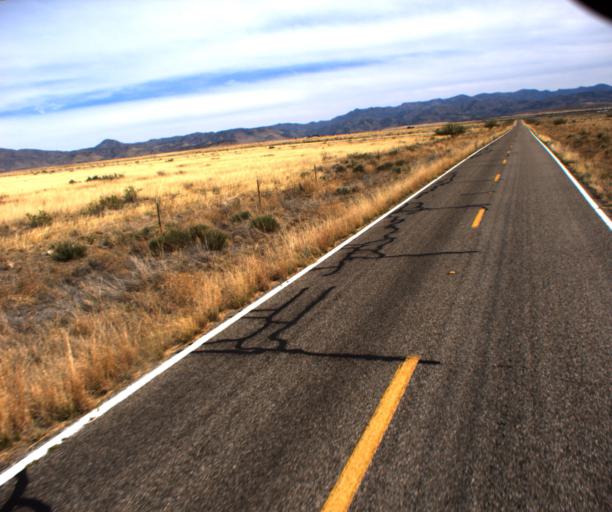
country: US
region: Arizona
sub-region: Cochise County
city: Willcox
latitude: 32.0445
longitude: -109.4854
